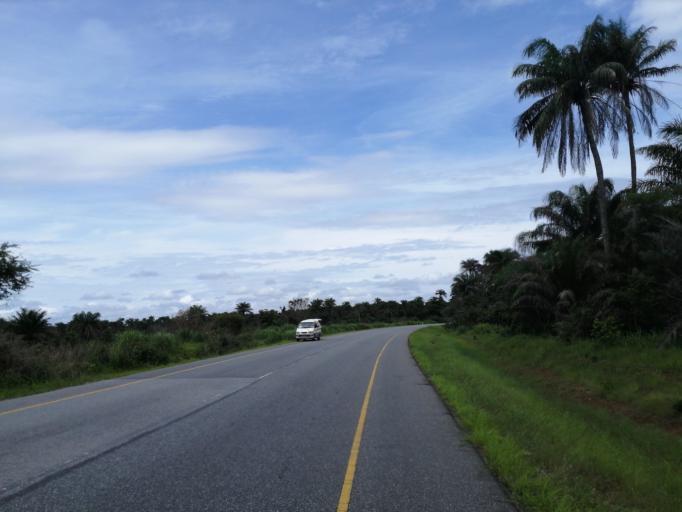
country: SL
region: Northern Province
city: Port Loko
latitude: 8.7500
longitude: -12.9187
